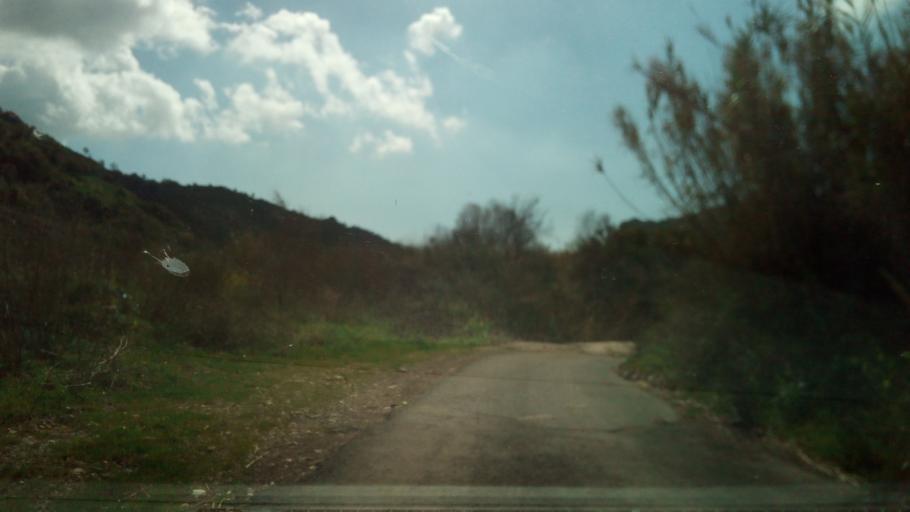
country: CY
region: Pafos
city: Mesogi
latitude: 34.8038
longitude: 32.5308
